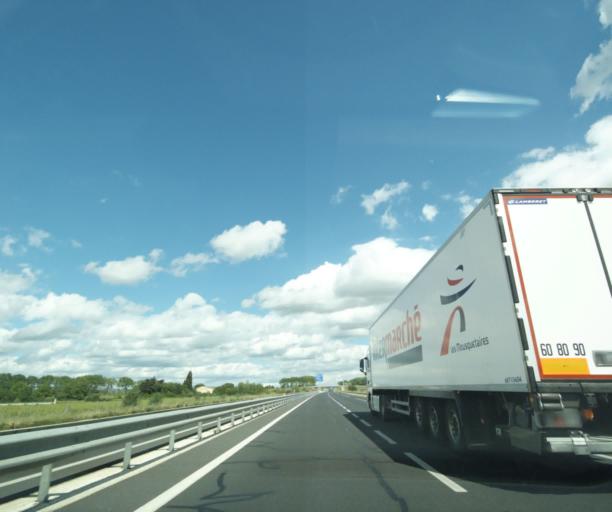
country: FR
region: Languedoc-Roussillon
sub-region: Departement de l'Herault
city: Saint-Andre-de-Sangonis
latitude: 43.6571
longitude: 3.4638
